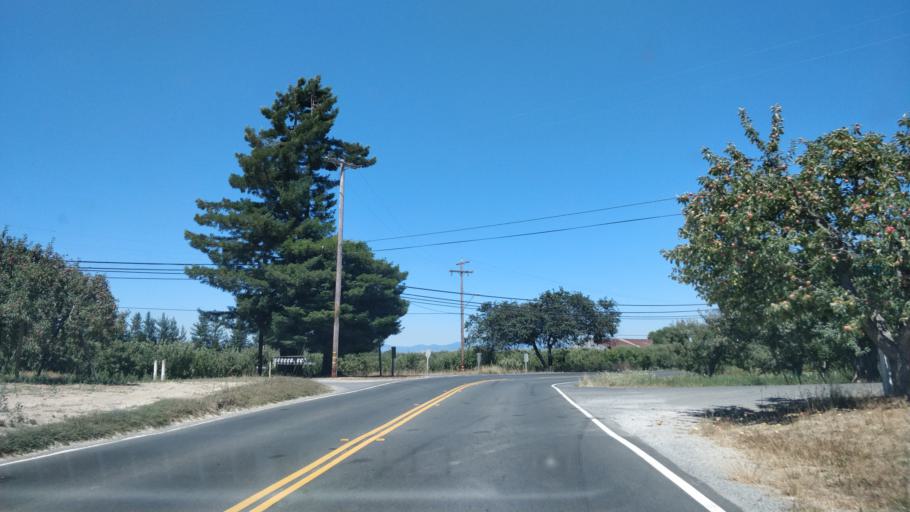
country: US
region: California
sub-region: Sonoma County
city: Sebastopol
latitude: 38.3958
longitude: -122.8613
